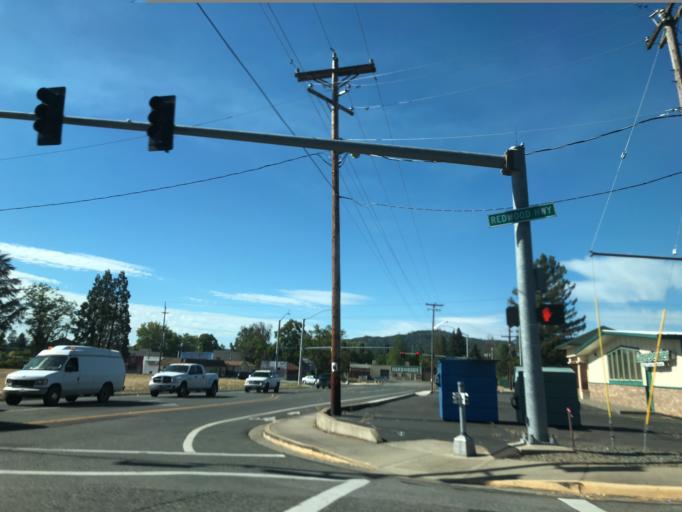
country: US
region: Oregon
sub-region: Josephine County
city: Grants Pass
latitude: 42.4215
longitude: -123.3512
